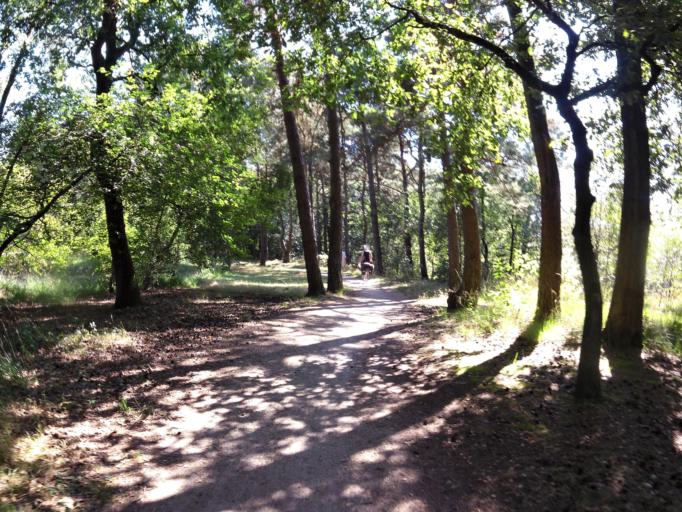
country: NL
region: Overijssel
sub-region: Gemeente Haaksbergen
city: Haaksbergen
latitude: 52.1522
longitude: 6.7988
